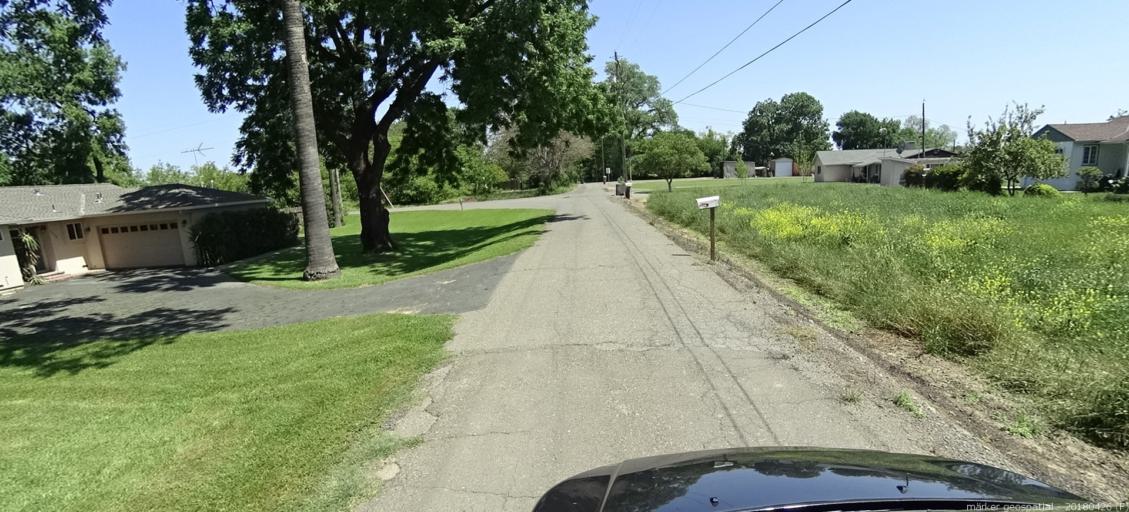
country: US
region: California
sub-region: Yolo County
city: West Sacramento
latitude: 38.5235
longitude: -121.5508
